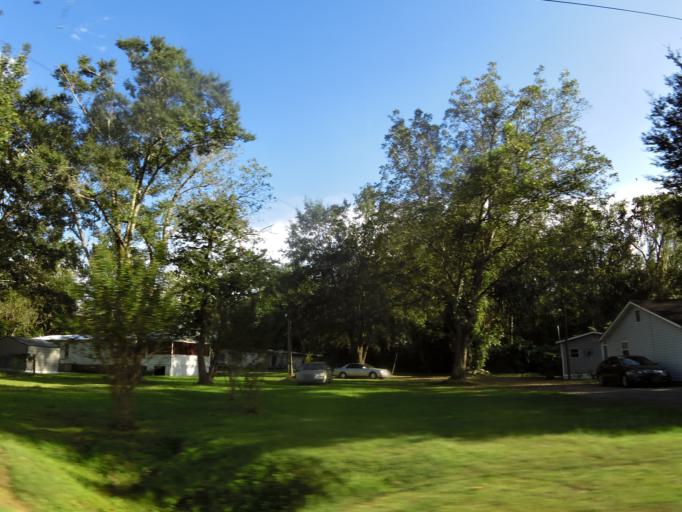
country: US
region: Georgia
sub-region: Brooks County
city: Quitman
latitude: 30.7768
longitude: -83.5648
